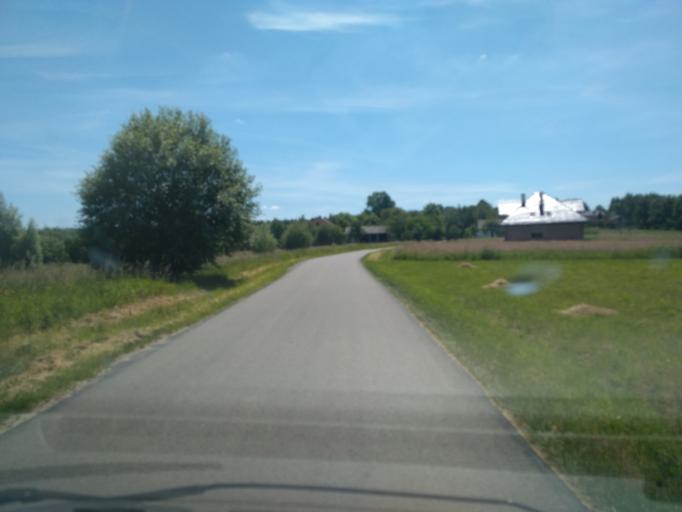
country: PL
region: Subcarpathian Voivodeship
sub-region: Powiat rzeszowski
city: Lubenia
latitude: 49.9168
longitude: 21.9155
